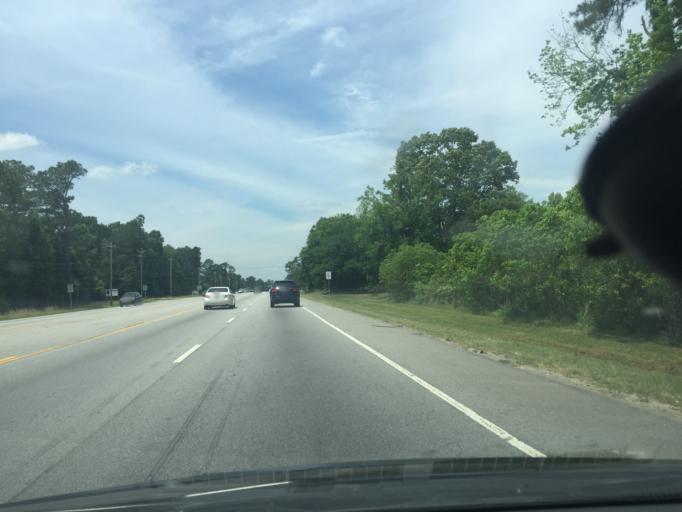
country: US
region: Georgia
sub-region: Chatham County
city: Bloomingdale
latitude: 32.1410
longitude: -81.3253
